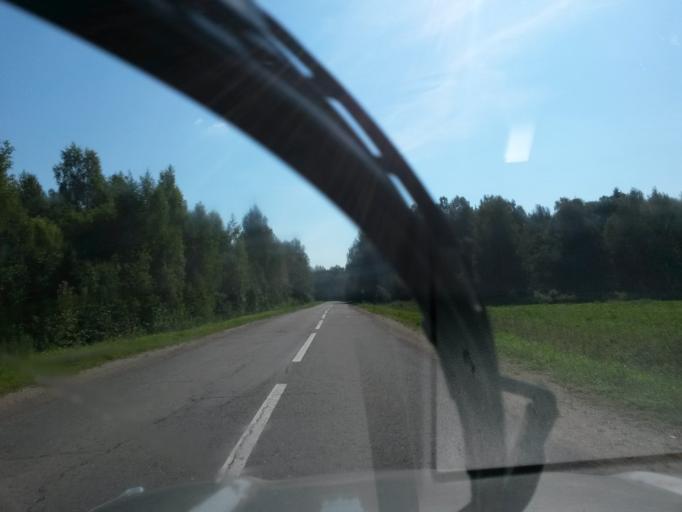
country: RU
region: Jaroslavl
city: Gavrilov-Yam
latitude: 57.3007
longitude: 40.0372
